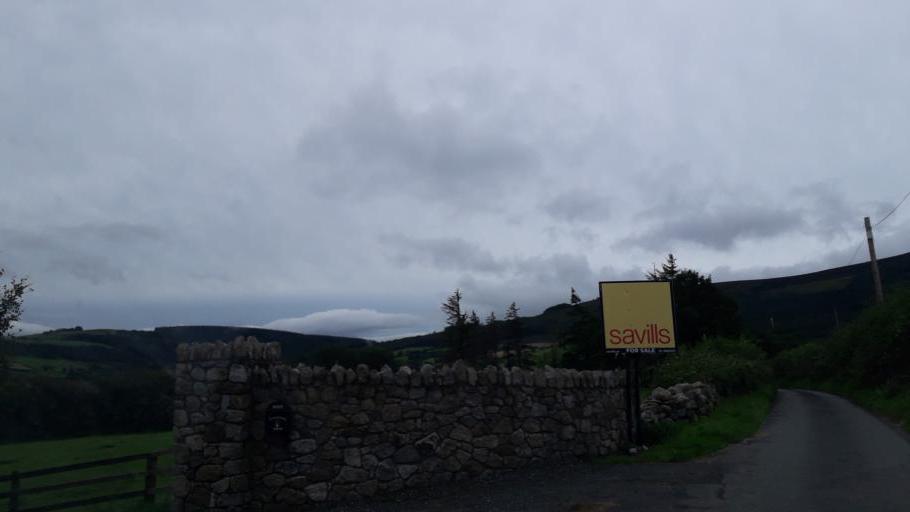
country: IE
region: Leinster
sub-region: Wicklow
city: Enniskerry
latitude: 53.1766
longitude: -6.2109
